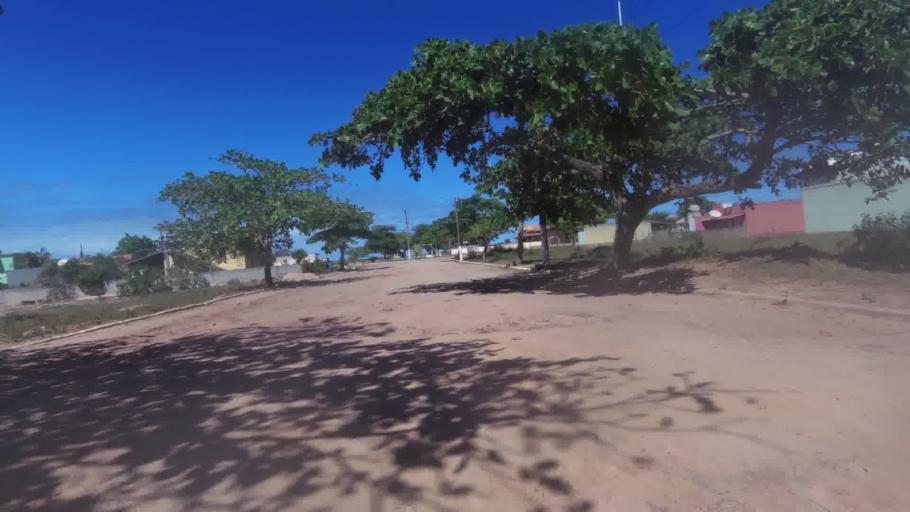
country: BR
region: Espirito Santo
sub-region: Marataizes
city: Marataizes
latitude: -21.1932
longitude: -40.9333
